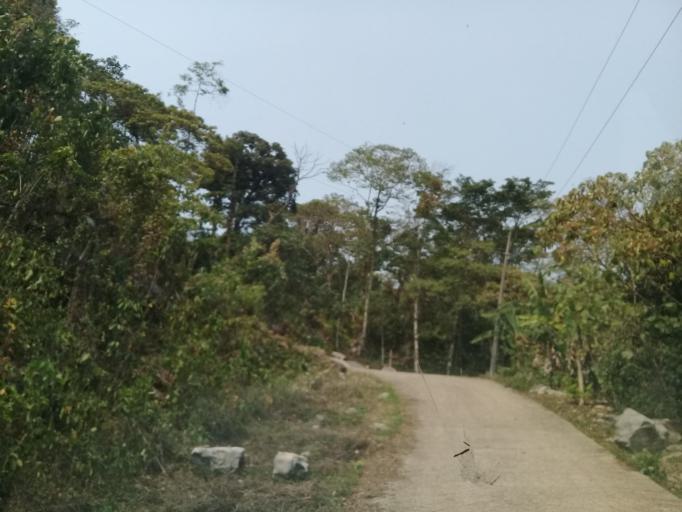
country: MX
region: Veracruz
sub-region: Tezonapa
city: Laguna Chica (Pueblo Nuevo)
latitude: 18.5859
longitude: -96.7462
